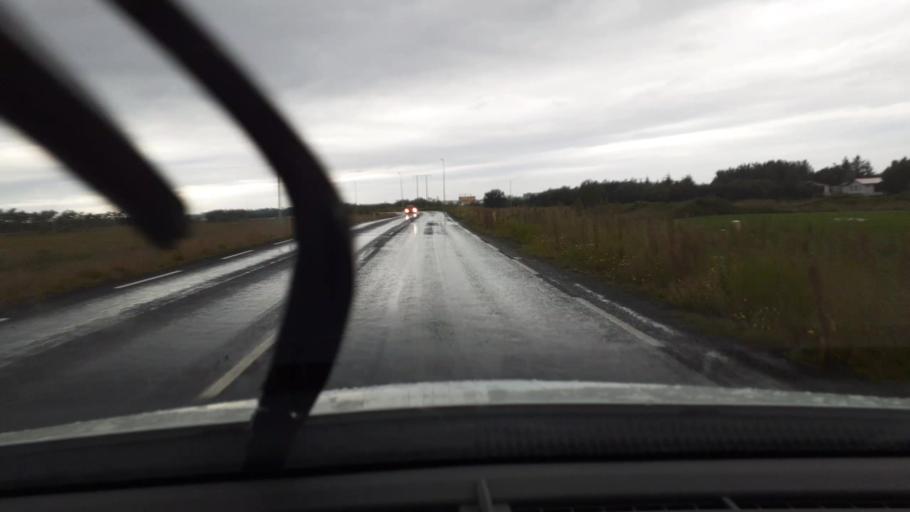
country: IS
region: West
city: Akranes
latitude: 64.3321
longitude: -22.0352
